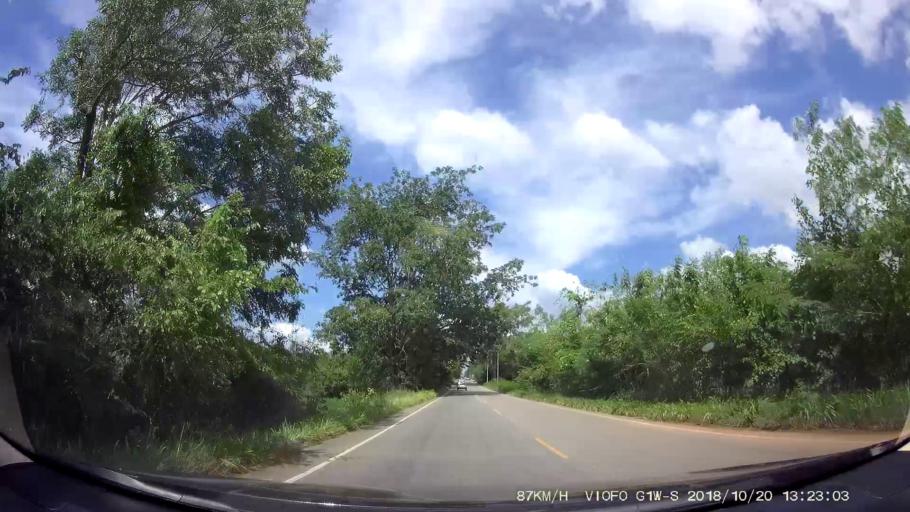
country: TH
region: Chaiyaphum
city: Khon San
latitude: 16.5792
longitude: 101.9194
